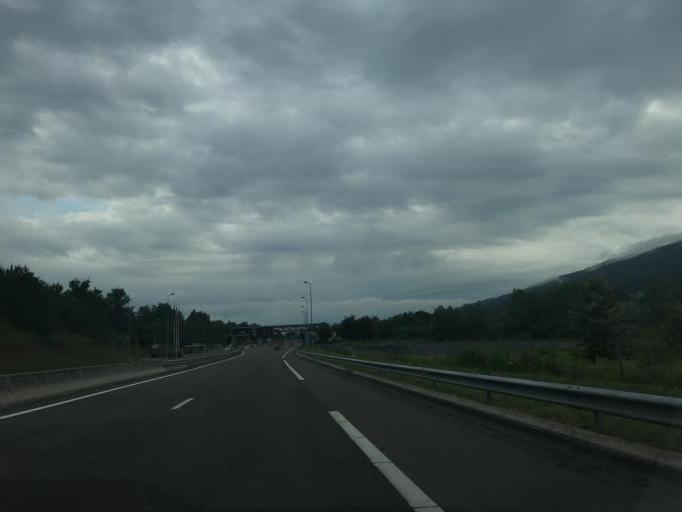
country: FR
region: Rhone-Alpes
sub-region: Departement de l'Ain
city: Groissiat
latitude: 46.2213
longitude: 5.6120
